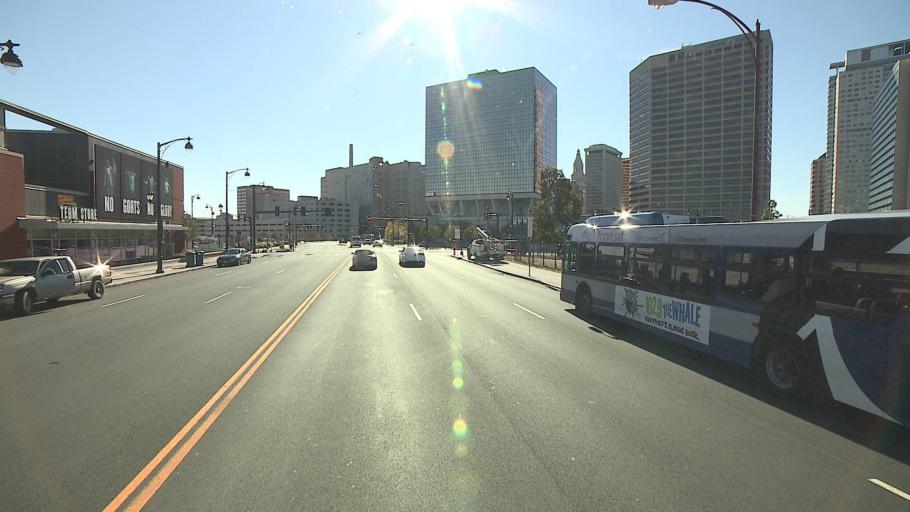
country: US
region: Connecticut
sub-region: Hartford County
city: Hartford
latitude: 41.7710
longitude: -72.6748
